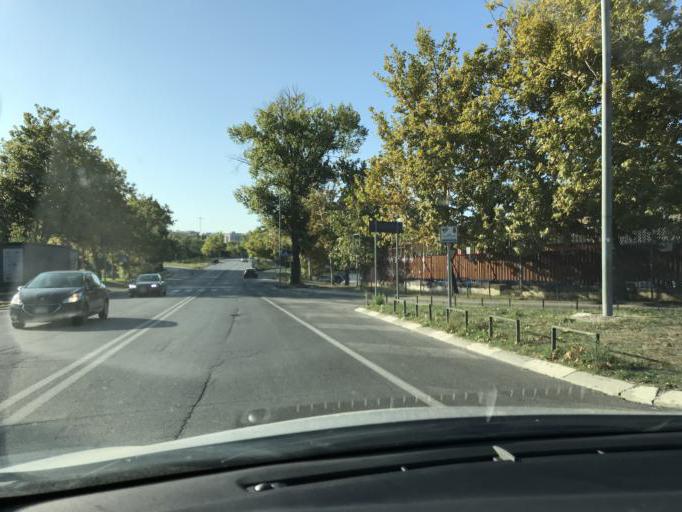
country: IT
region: Umbria
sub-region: Provincia di Perugia
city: Lacugnano
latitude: 43.1079
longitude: 12.3582
